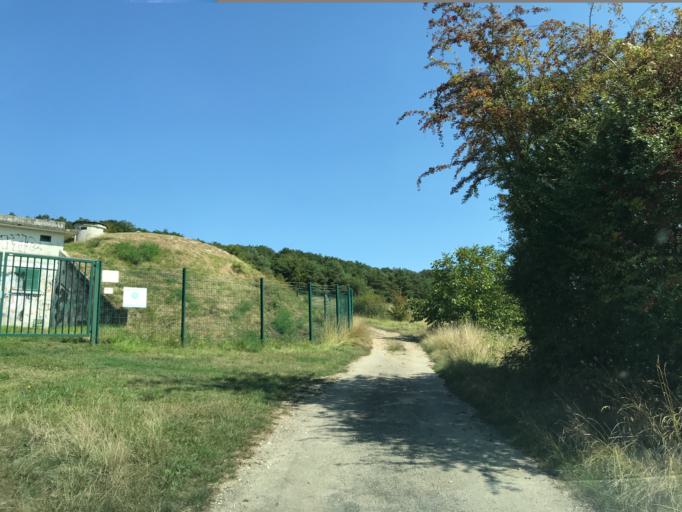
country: FR
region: Haute-Normandie
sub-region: Departement de l'Eure
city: Heudreville-sur-Eure
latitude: 49.1284
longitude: 1.2307
